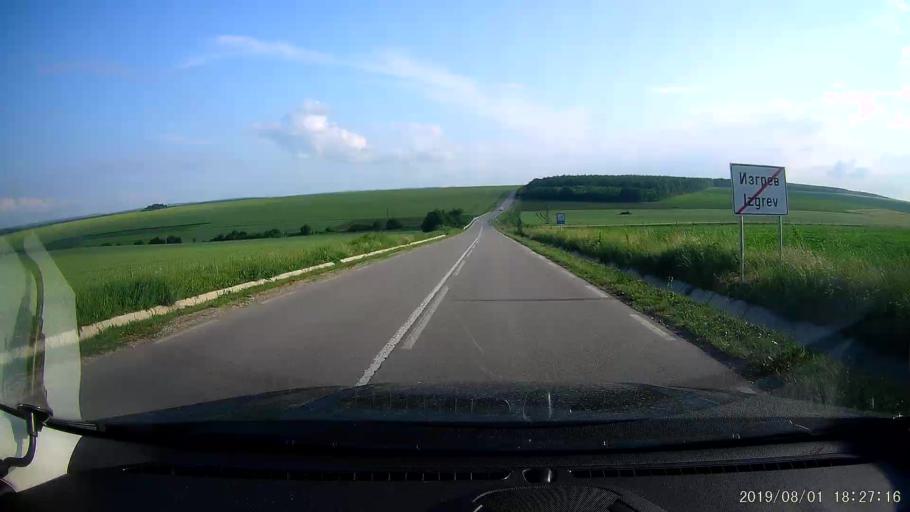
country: BG
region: Shumen
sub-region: Obshtina Venets
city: Venets
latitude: 43.5901
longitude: 26.9833
